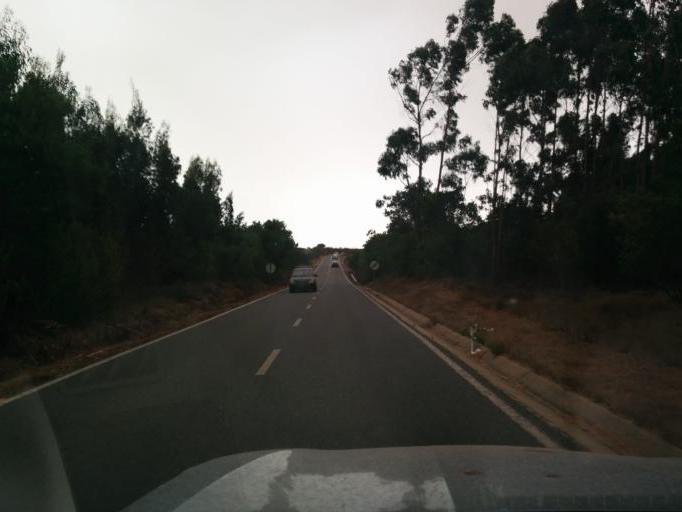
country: PT
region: Beja
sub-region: Odemira
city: Sao Teotonio
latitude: 37.5459
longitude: -8.7462
